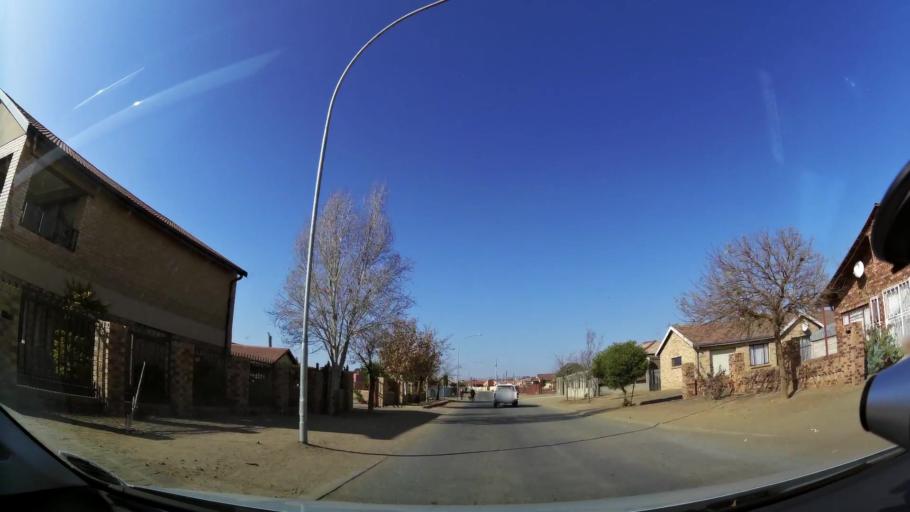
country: ZA
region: Orange Free State
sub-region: Mangaung Metropolitan Municipality
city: Bloemfontein
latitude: -29.1906
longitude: 26.2235
